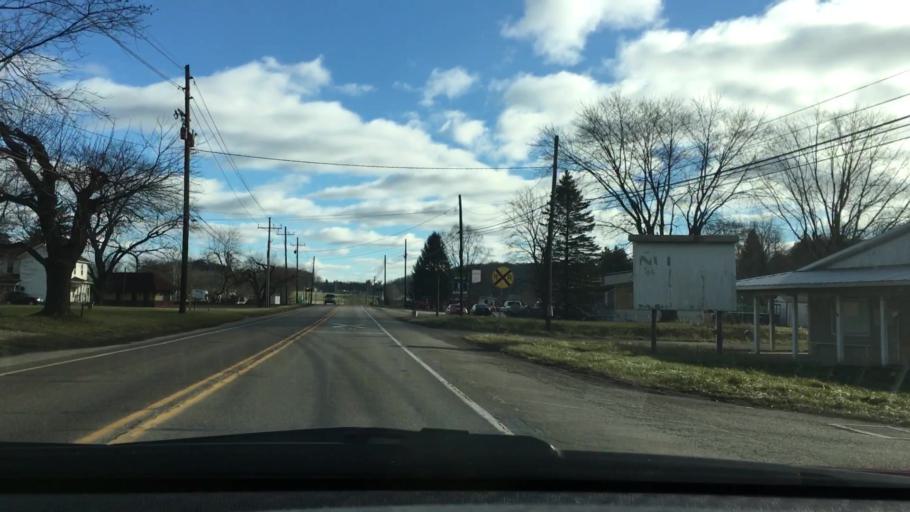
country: US
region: Pennsylvania
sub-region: Indiana County
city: Indiana
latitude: 40.6541
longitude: -79.2867
